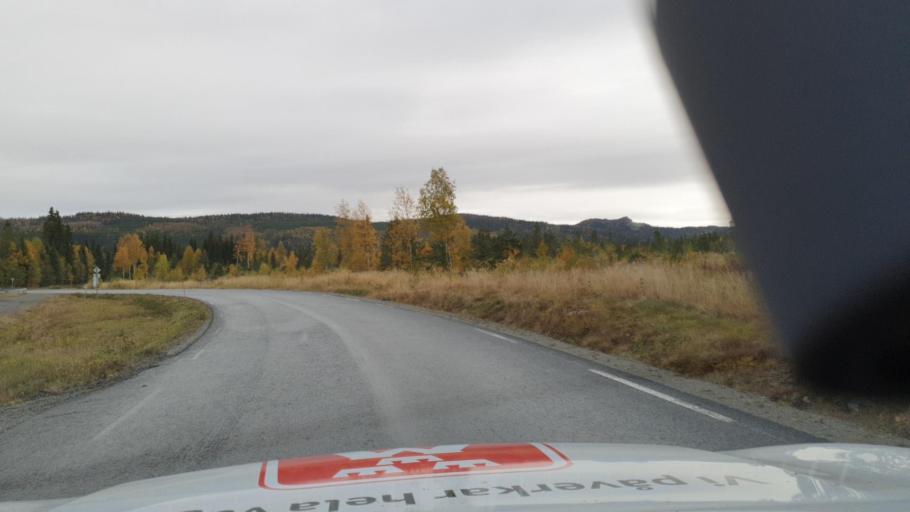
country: NO
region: Nord-Trondelag
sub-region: Lierne
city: Sandvika
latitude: 64.4856
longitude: 13.9534
